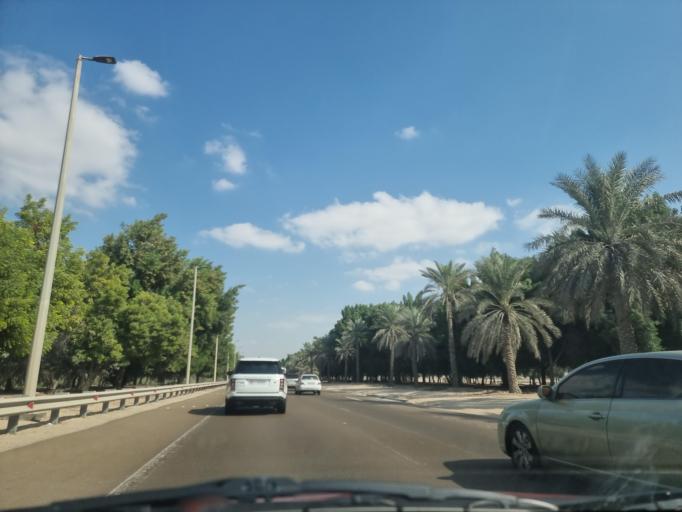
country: AE
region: Abu Dhabi
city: Abu Dhabi
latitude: 24.4083
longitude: 54.6288
